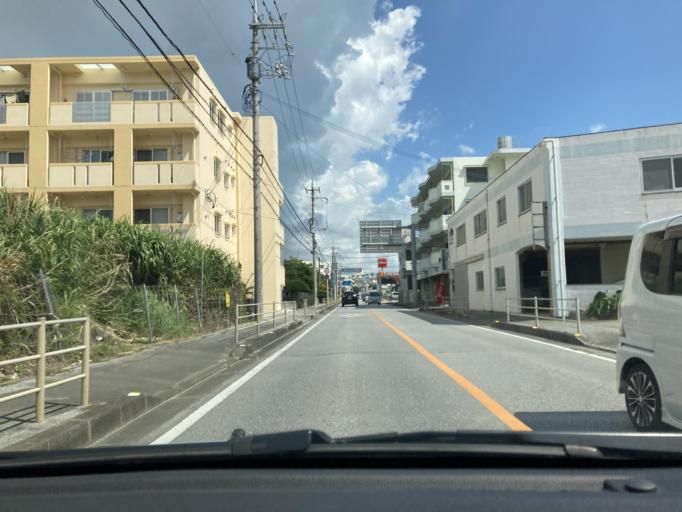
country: JP
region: Okinawa
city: Tomigusuku
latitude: 26.1831
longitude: 127.7258
